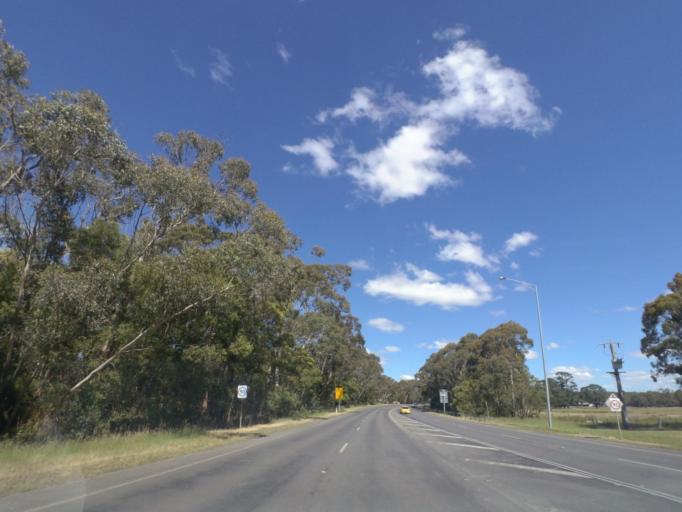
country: AU
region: Victoria
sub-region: Hume
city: Sunbury
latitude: -37.4322
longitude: 144.5602
